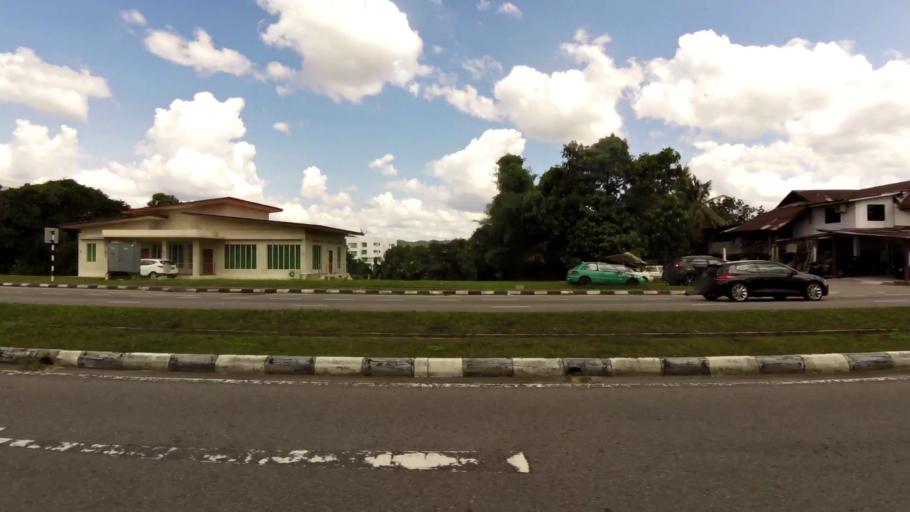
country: BN
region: Brunei and Muara
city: Bandar Seri Begawan
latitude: 4.9473
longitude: 114.9586
